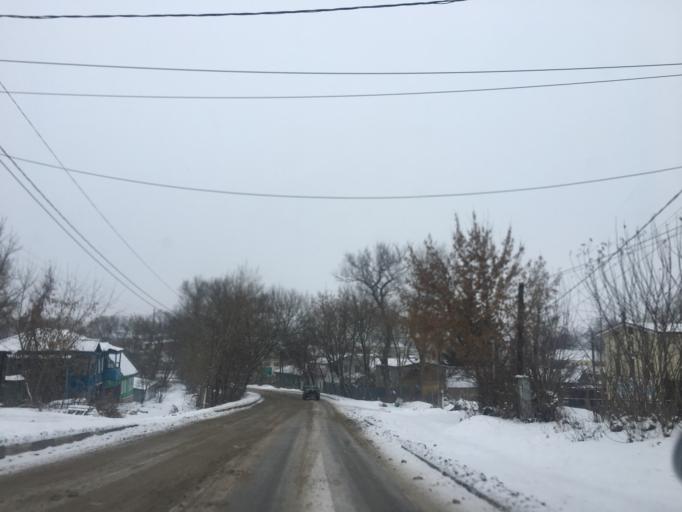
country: RU
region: Tula
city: Tula
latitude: 54.1917
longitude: 37.5761
